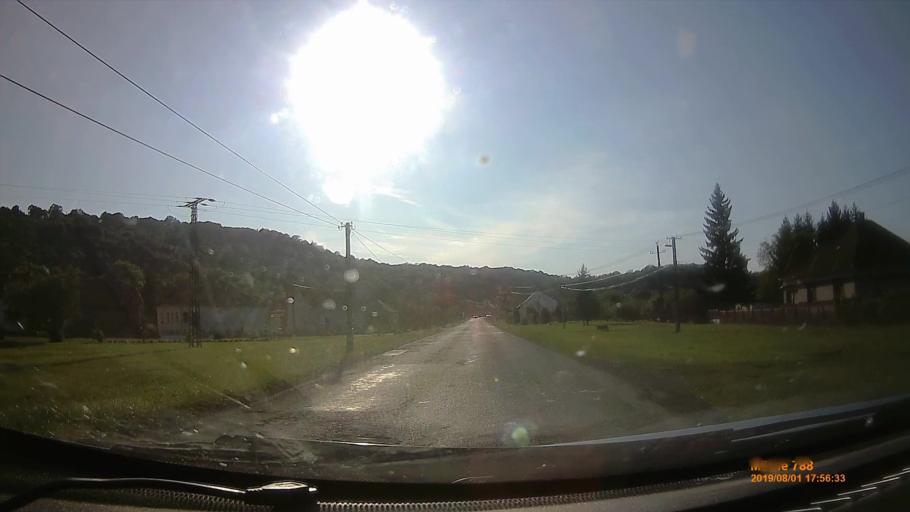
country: HU
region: Baranya
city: Sasd
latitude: 46.1977
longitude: 18.1219
